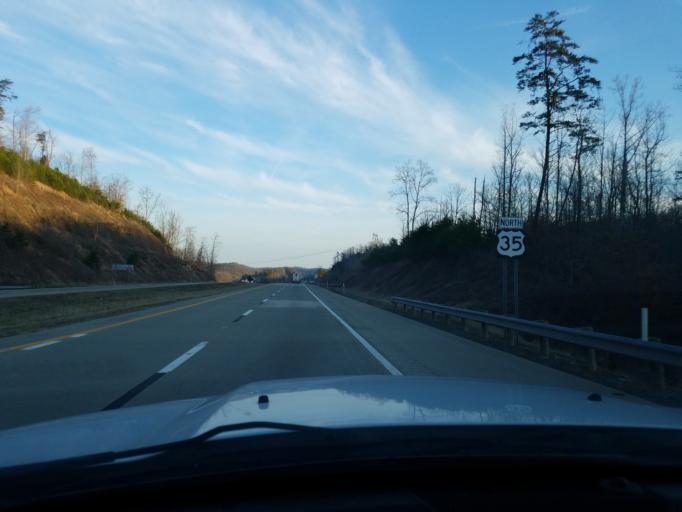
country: US
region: West Virginia
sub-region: Putnam County
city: Eleanor
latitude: 38.5039
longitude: -81.9309
